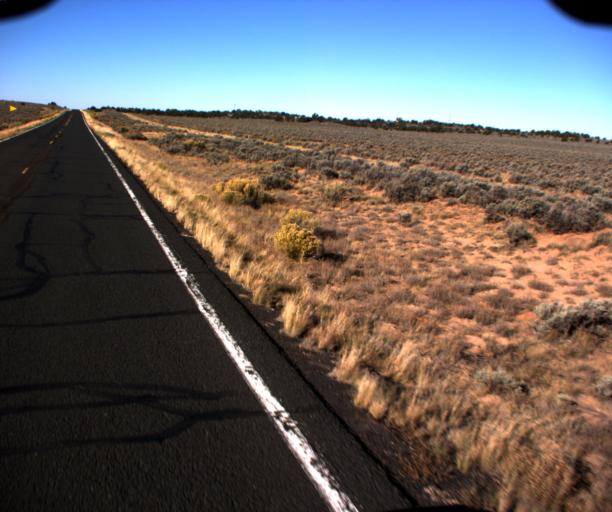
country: US
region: Arizona
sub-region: Navajo County
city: First Mesa
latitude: 35.7437
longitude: -110.0642
